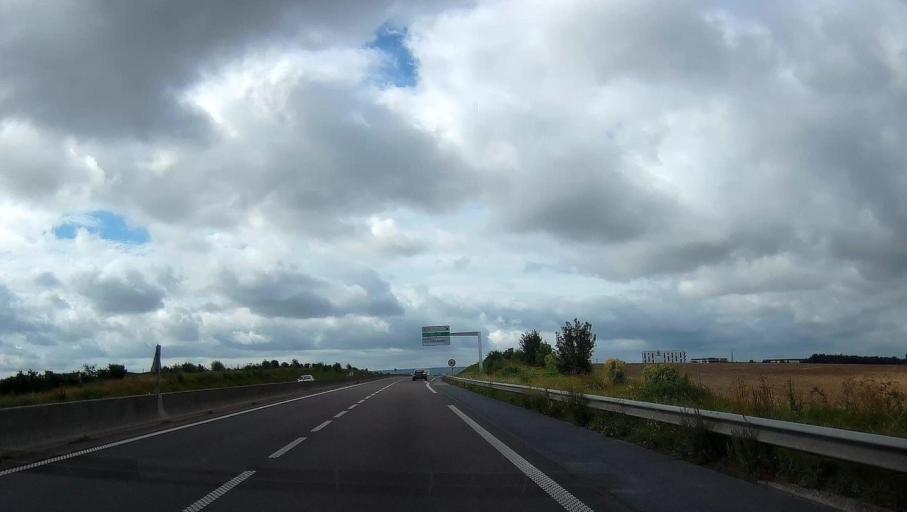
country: FR
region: Champagne-Ardenne
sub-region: Departement de la Marne
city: Cernay-les-Reims
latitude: 49.2471
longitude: 4.0820
